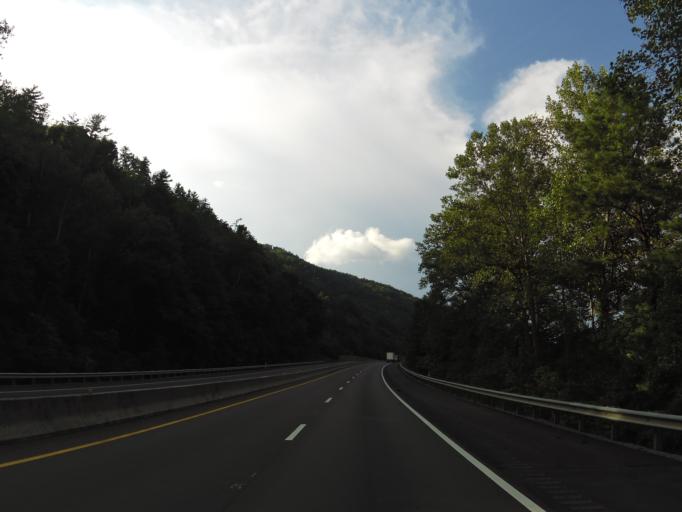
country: US
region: Tennessee
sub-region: Cocke County
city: Newport
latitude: 35.8201
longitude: -83.1814
